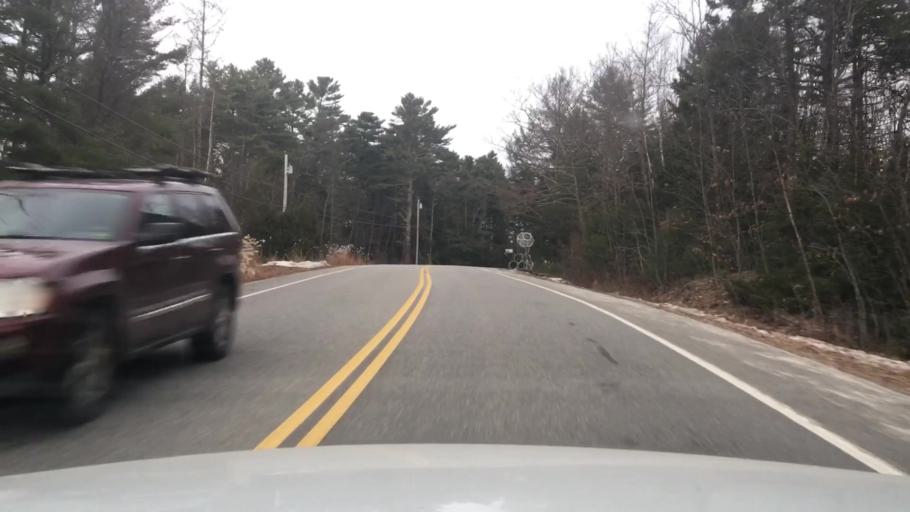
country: US
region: Maine
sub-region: Cumberland County
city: Freeport
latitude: 43.8604
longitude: -70.0740
